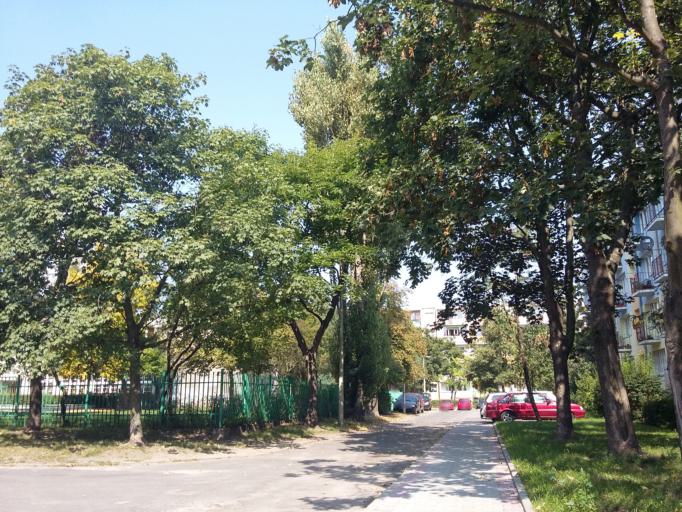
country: PL
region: Lodz Voivodeship
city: Lodz
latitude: 51.7455
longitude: 19.4149
